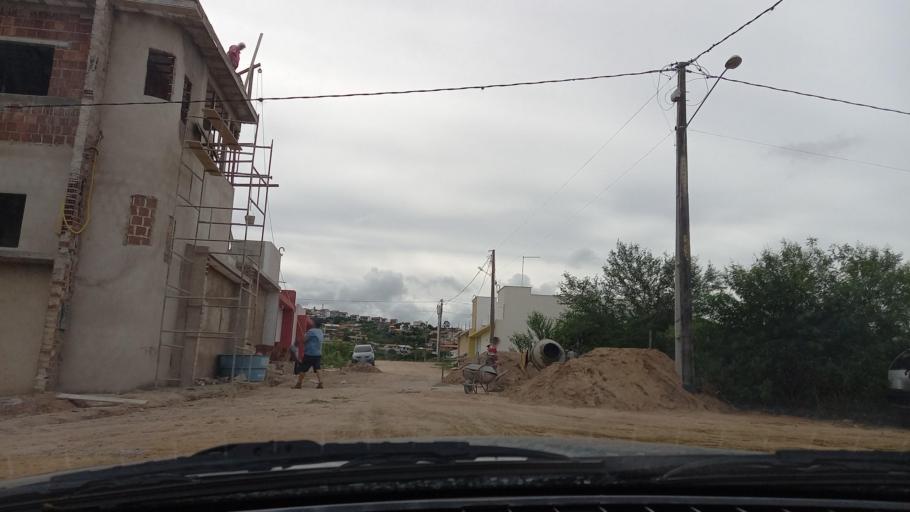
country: BR
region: Pernambuco
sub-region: Gravata
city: Gravata
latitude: -8.2252
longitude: -35.5755
